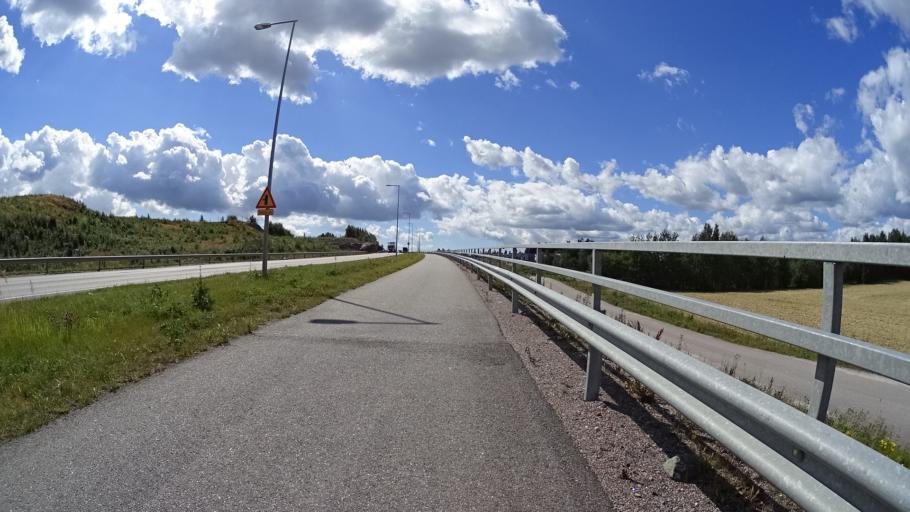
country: FI
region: Uusimaa
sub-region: Helsinki
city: Teekkarikylae
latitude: 60.3123
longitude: 24.8930
